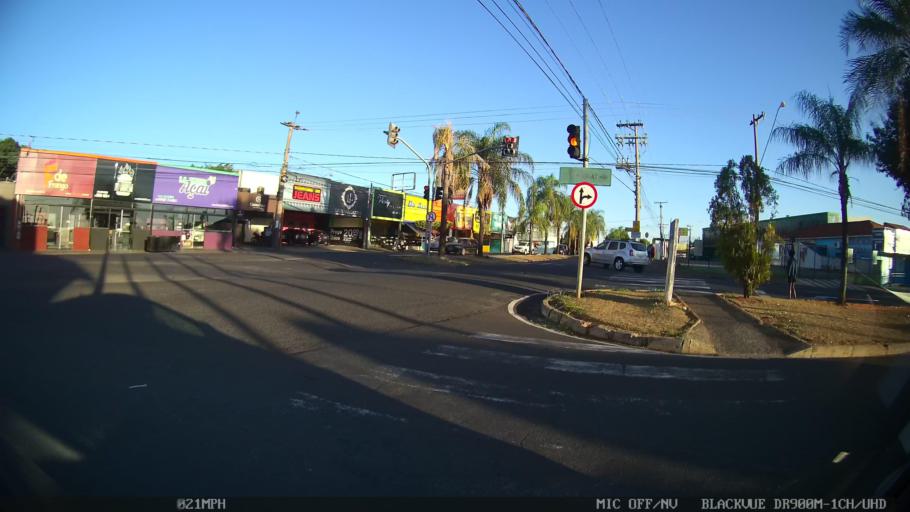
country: BR
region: Sao Paulo
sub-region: Sao Jose Do Rio Preto
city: Sao Jose do Rio Preto
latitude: -20.7798
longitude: -49.3682
